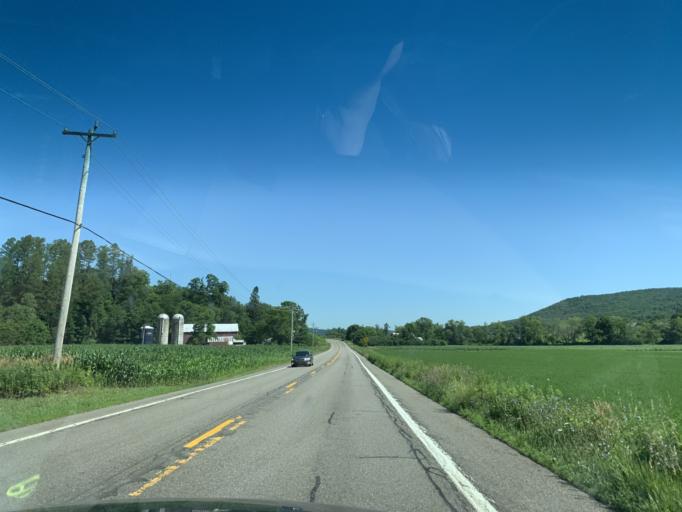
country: US
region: New York
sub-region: Chenango County
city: Norwich
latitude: 42.4922
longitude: -75.4005
